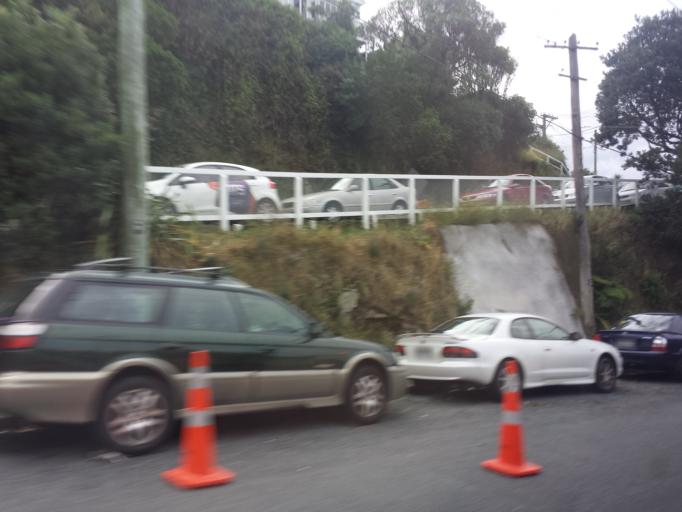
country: NZ
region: Wellington
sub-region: Wellington City
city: Wellington
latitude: -41.3027
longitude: 174.7926
